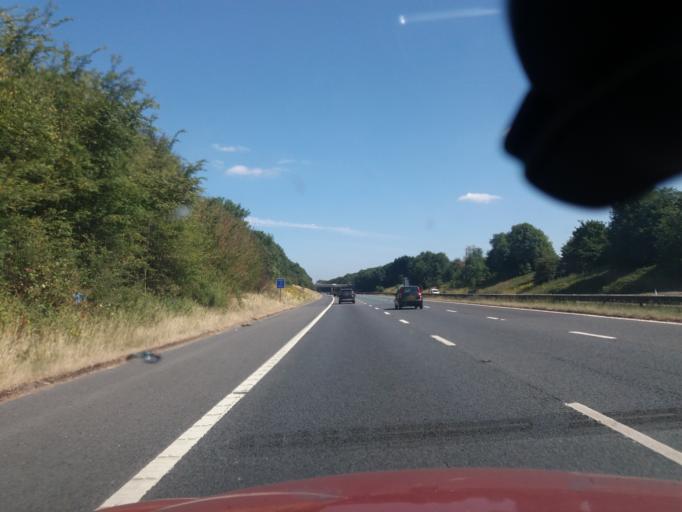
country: GB
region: England
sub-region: Borough of Wigan
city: Atherton
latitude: 53.5507
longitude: -2.4757
